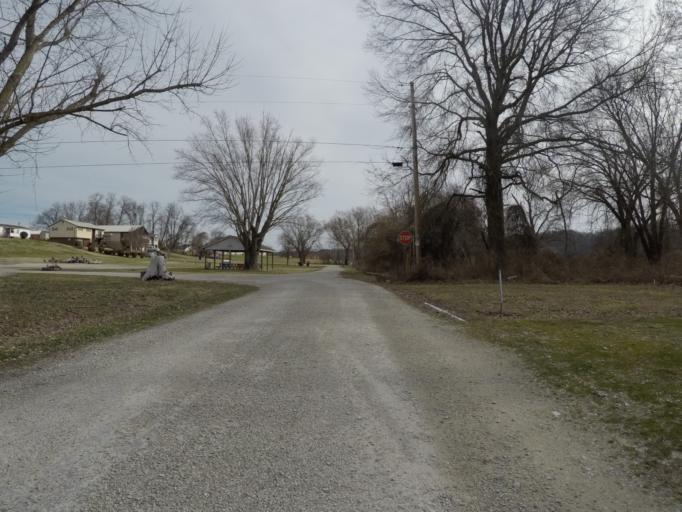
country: US
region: West Virginia
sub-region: Cabell County
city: Pea Ridge
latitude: 38.4392
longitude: -82.3650
